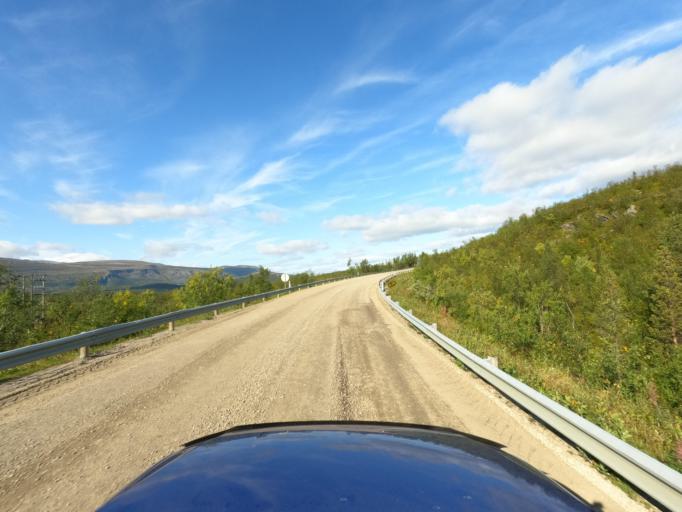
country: NO
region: Finnmark Fylke
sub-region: Porsanger
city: Lakselv
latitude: 69.8800
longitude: 25.0227
